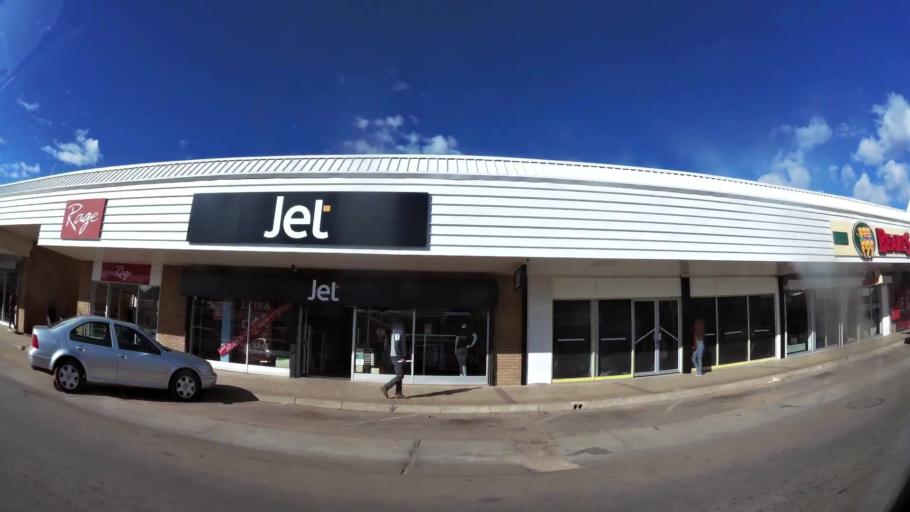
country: ZA
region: Limpopo
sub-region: Waterberg District Municipality
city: Bela-Bela
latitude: -24.8850
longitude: 28.2951
